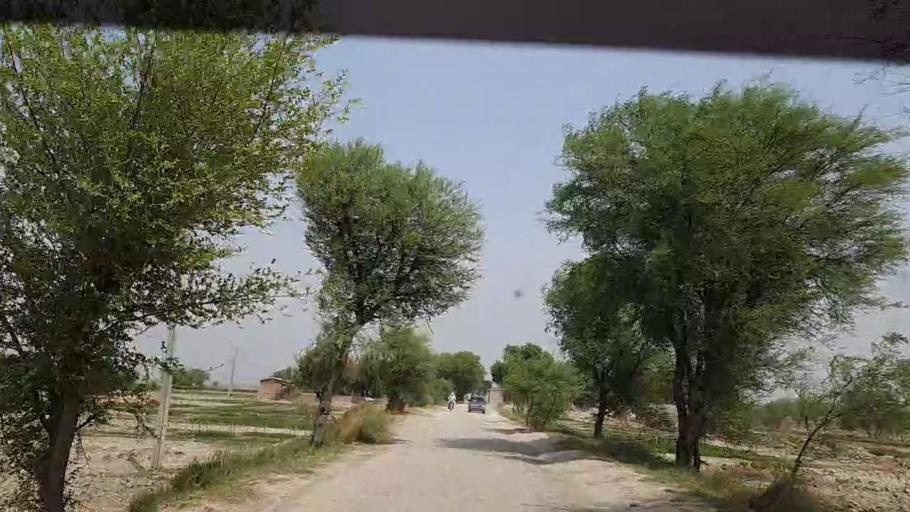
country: PK
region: Sindh
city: Khairpur Nathan Shah
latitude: 27.0783
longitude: 67.6855
